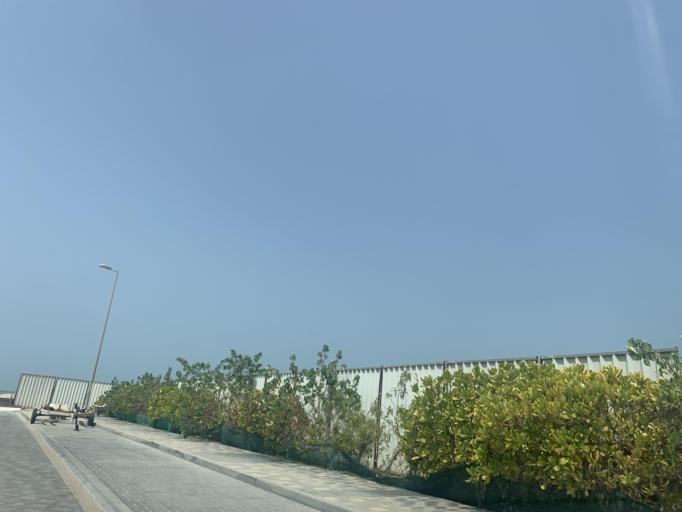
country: BH
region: Muharraq
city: Al Hadd
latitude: 26.2755
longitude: 50.6719
